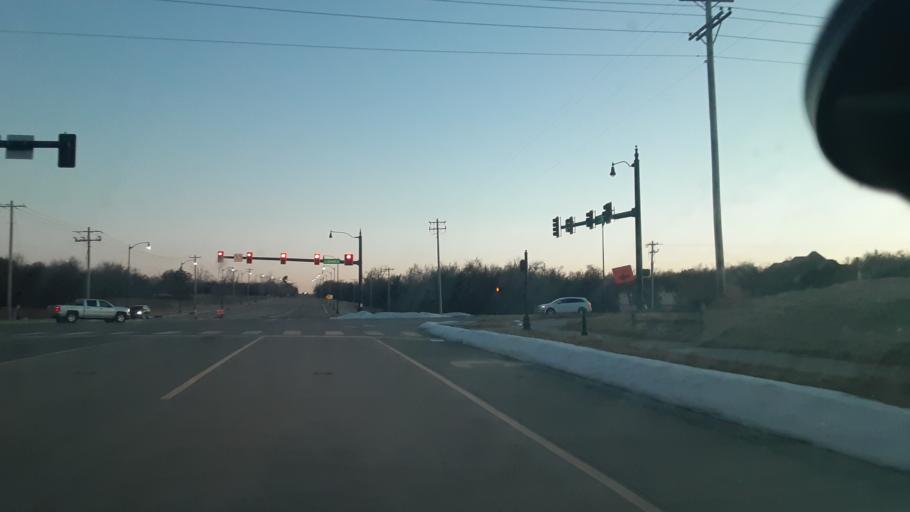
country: US
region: Oklahoma
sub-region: Oklahoma County
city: Edmond
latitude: 35.6822
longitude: -97.4252
